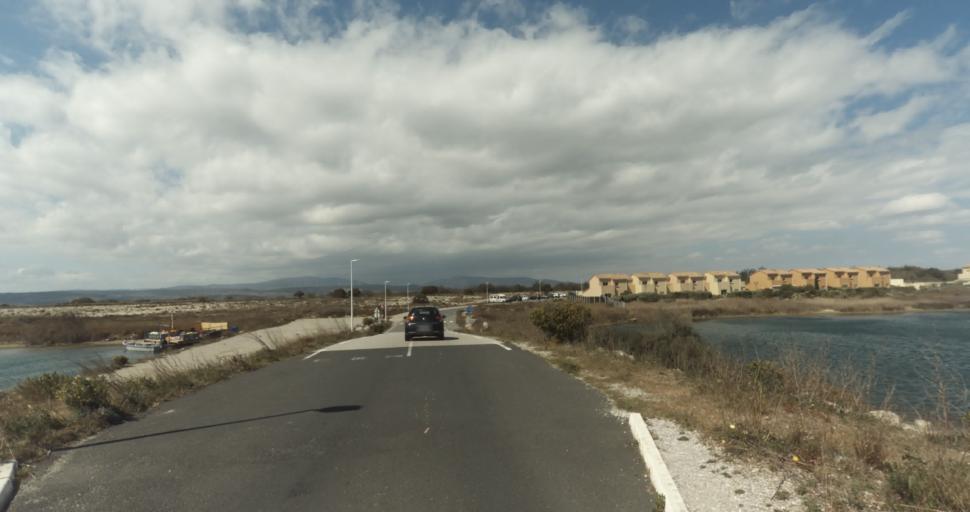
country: FR
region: Languedoc-Roussillon
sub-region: Departement de l'Aude
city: Leucate
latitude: 42.8779
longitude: 3.0448
